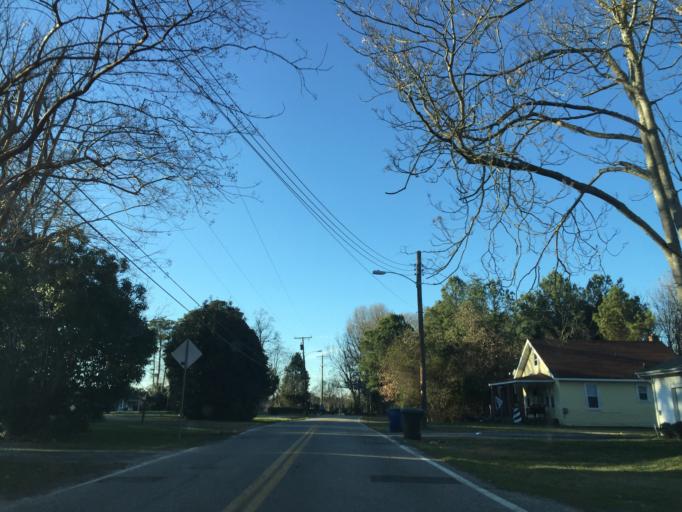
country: US
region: Virginia
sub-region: Isle of Wight County
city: Carrollton
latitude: 37.0785
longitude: -76.5228
